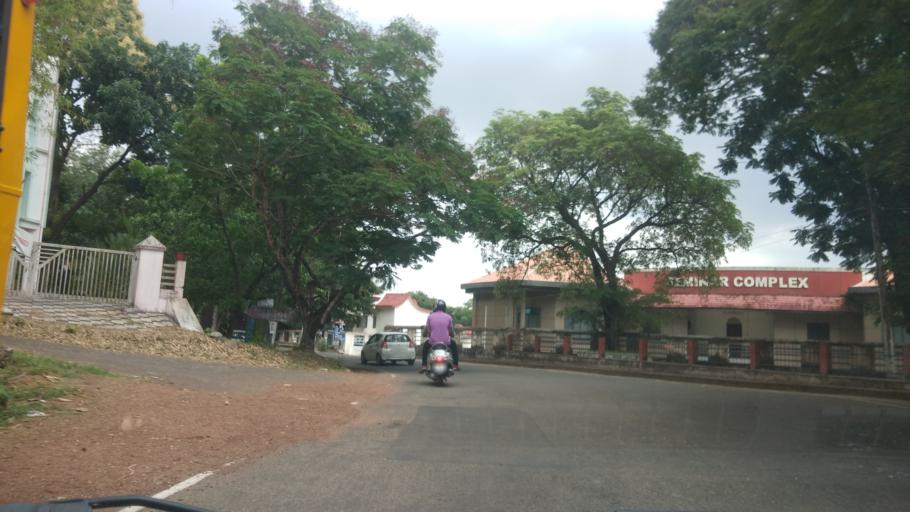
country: IN
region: Kerala
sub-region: Ernakulam
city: Elur
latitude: 10.0443
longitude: 76.3246
